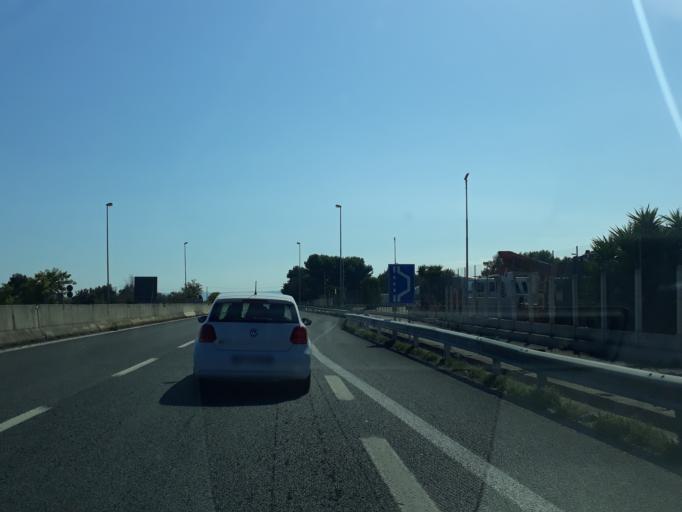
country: IT
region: Apulia
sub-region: Provincia di Bari
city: Monopoli
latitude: 40.9174
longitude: 17.3188
